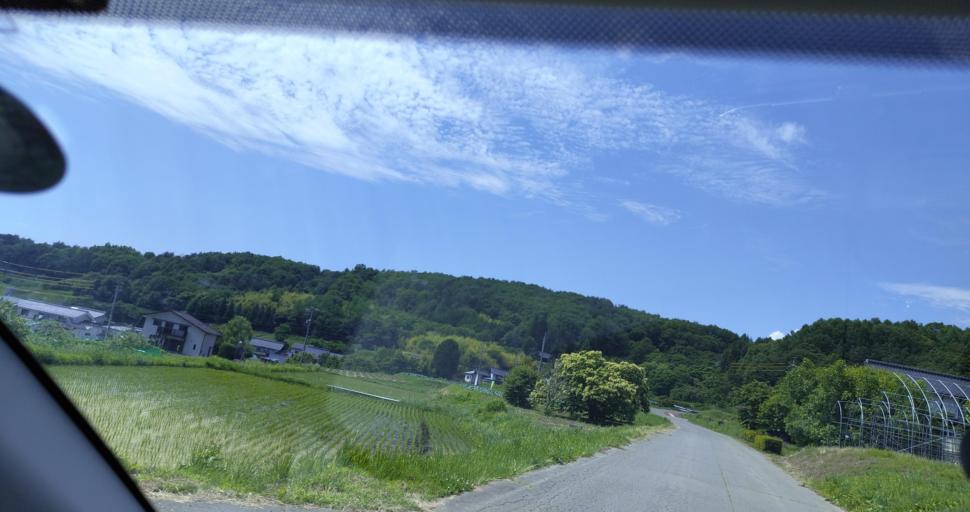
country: JP
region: Nagano
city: Ueda
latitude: 36.3905
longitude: 138.3332
